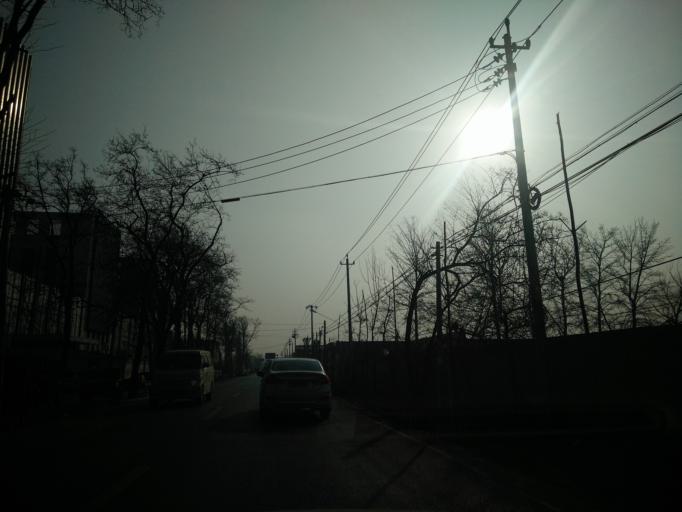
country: CN
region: Beijing
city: Xingfeng
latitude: 39.7255
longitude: 116.3722
